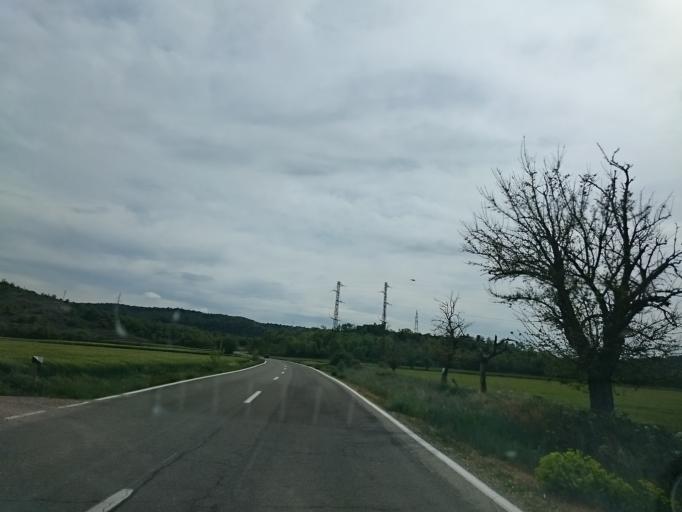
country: ES
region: Catalonia
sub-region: Provincia de Lleida
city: Tora de Riubregos
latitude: 41.8016
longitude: 1.4034
